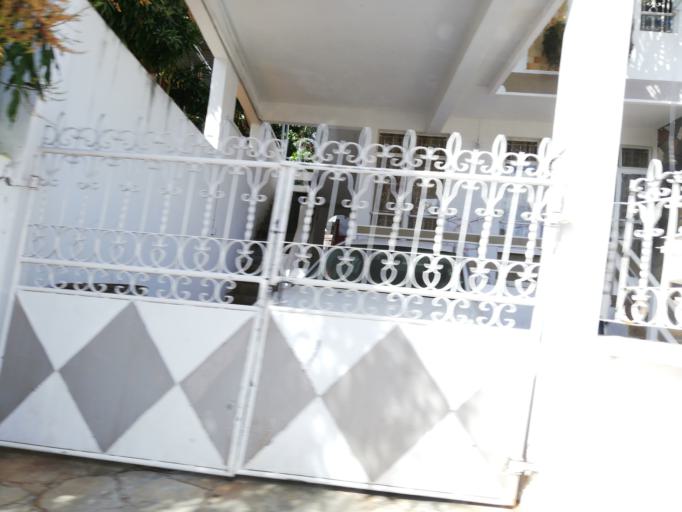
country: MU
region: Black River
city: Petite Riviere
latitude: -20.1941
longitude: 57.4661
